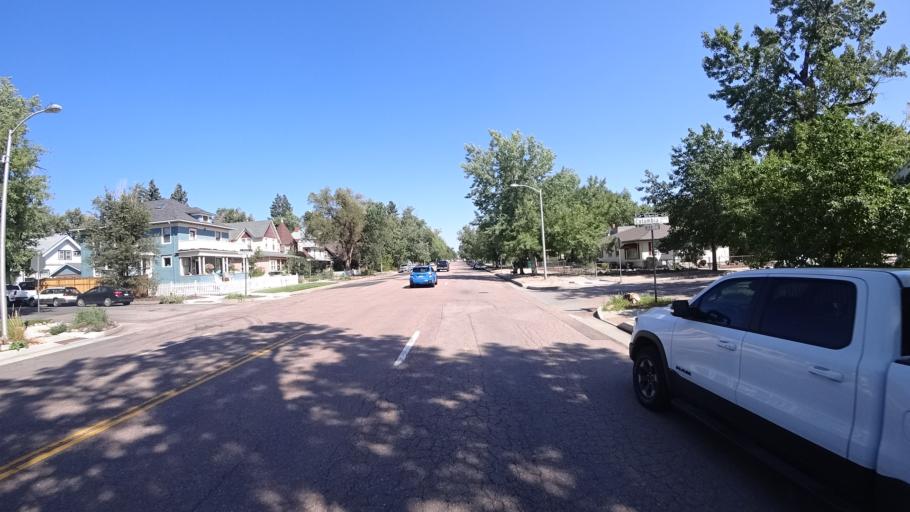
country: US
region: Colorado
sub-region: El Paso County
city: Colorado Springs
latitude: 38.8535
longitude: -104.8188
